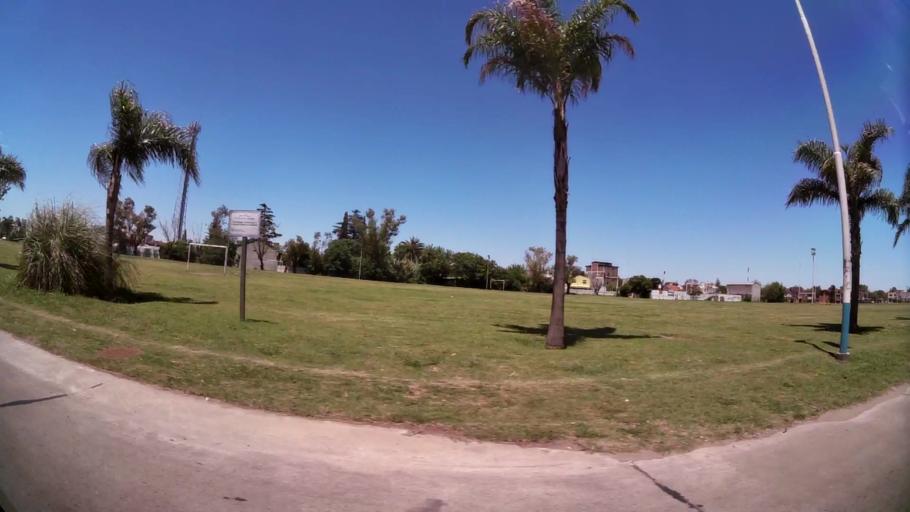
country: AR
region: Buenos Aires
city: Hurlingham
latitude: -34.4984
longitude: -58.6989
